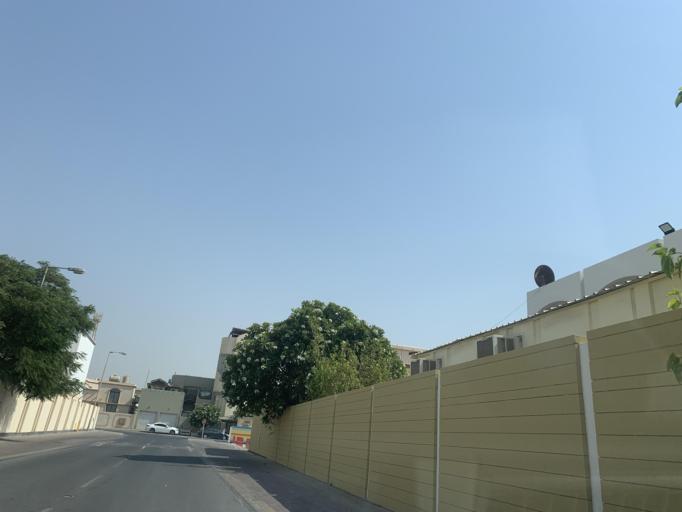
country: BH
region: Manama
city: Jidd Hafs
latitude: 26.2034
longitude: 50.5285
